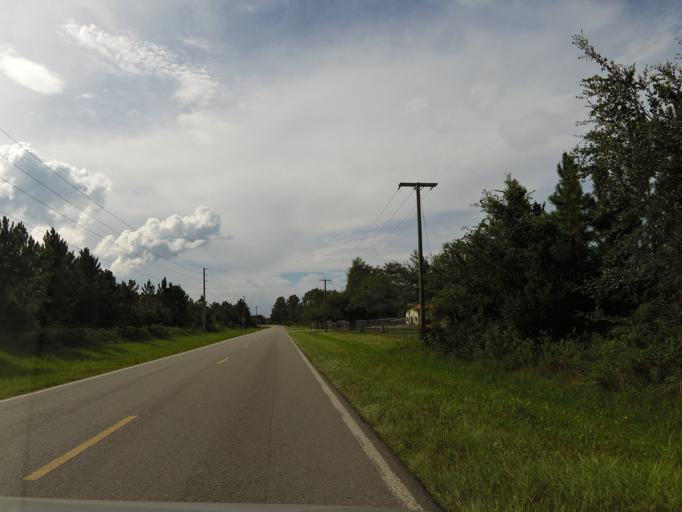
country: US
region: Florida
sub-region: Clay County
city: Green Cove Springs
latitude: 29.9582
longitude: -81.6687
